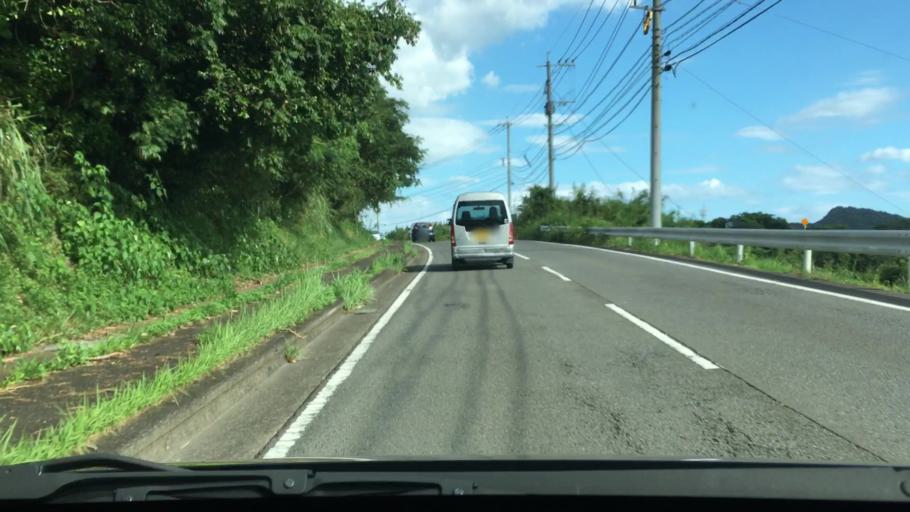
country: JP
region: Nagasaki
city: Togitsu
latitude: 32.8206
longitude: 129.7352
